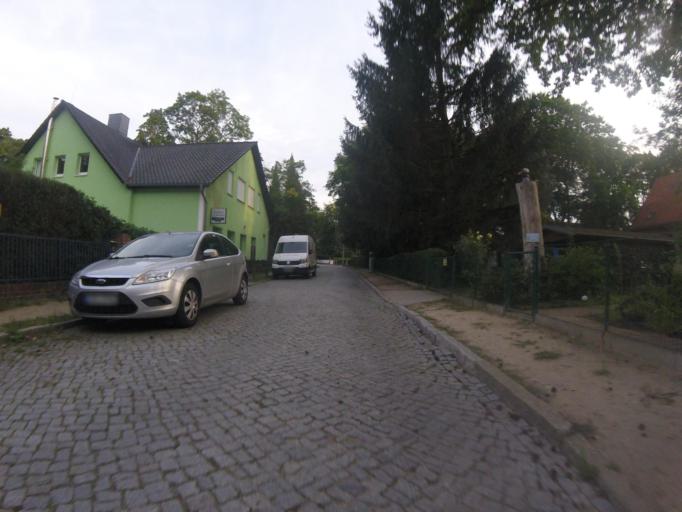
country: DE
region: Brandenburg
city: Zeuthen
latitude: 52.3492
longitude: 13.6104
